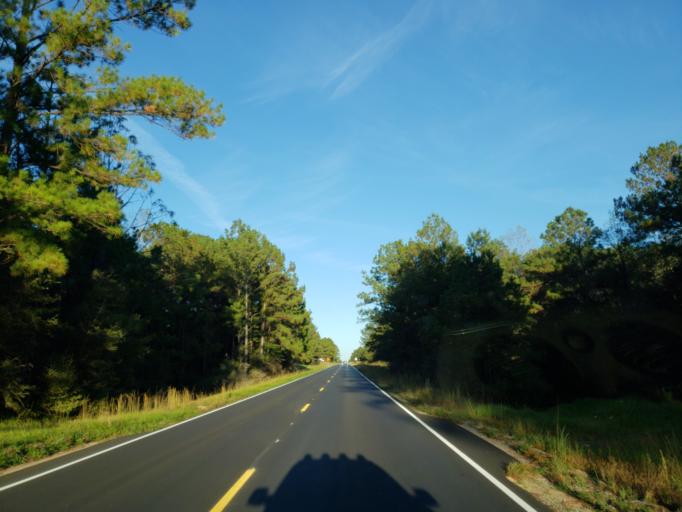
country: US
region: Mississippi
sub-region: Wayne County
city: Belmont
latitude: 31.4136
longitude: -88.5951
